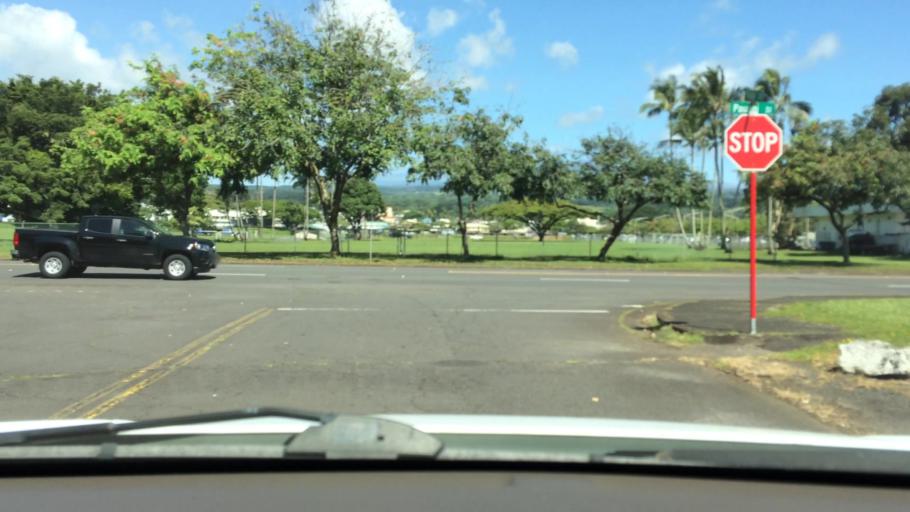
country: US
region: Hawaii
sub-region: Hawaii County
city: Hilo
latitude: 19.7213
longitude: -155.0784
